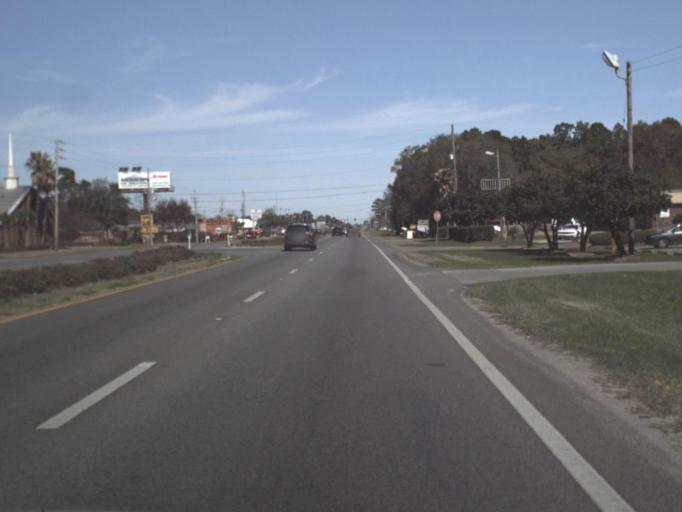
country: US
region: Florida
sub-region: Bay County
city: Hiland Park
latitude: 30.1976
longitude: -85.6496
